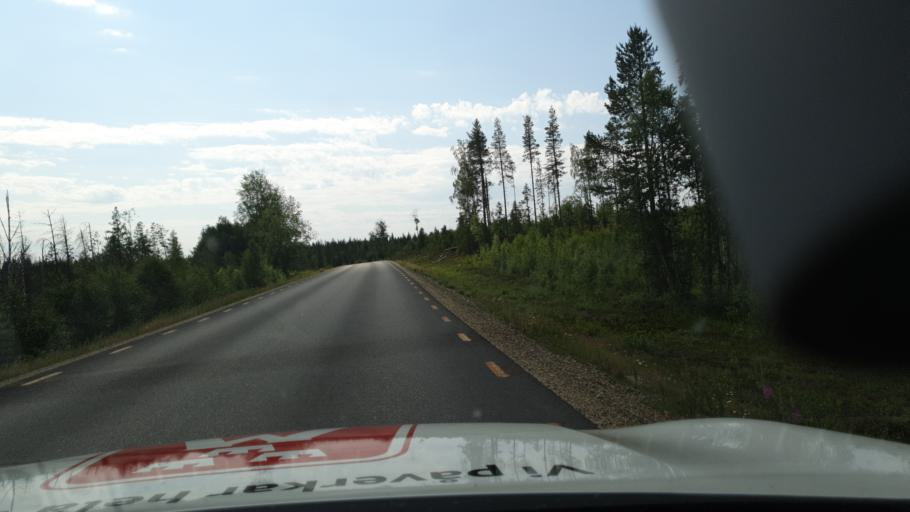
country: SE
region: Vaesterbotten
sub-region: Vindelns Kommun
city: Vindeln
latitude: 64.4246
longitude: 19.3531
